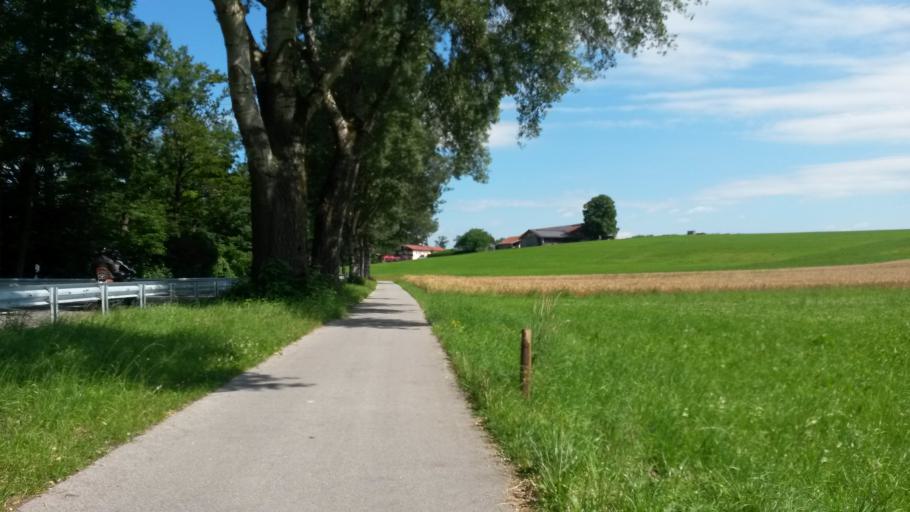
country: DE
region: Bavaria
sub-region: Upper Bavaria
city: Grabenstatt
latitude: 47.8609
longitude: 12.5281
